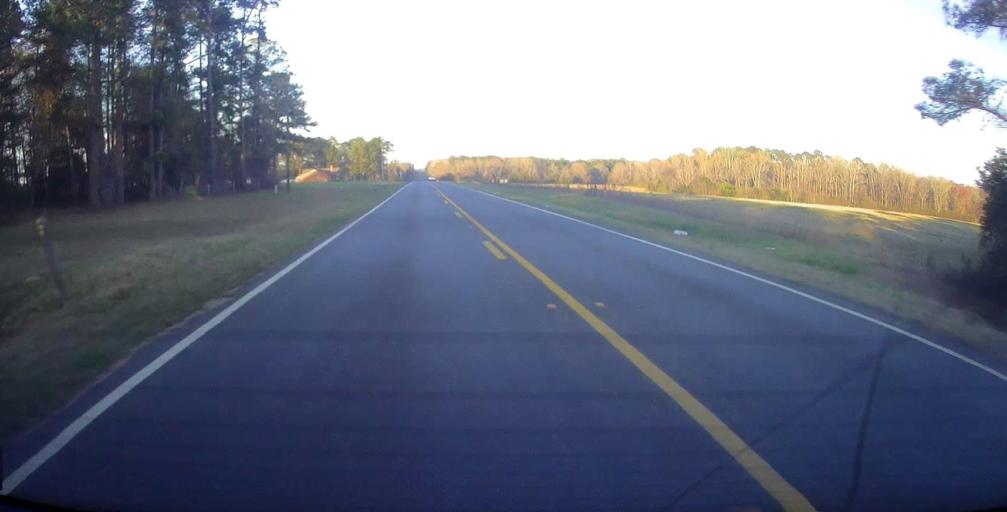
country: US
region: Georgia
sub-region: Laurens County
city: Dublin
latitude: 32.4123
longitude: -82.9585
